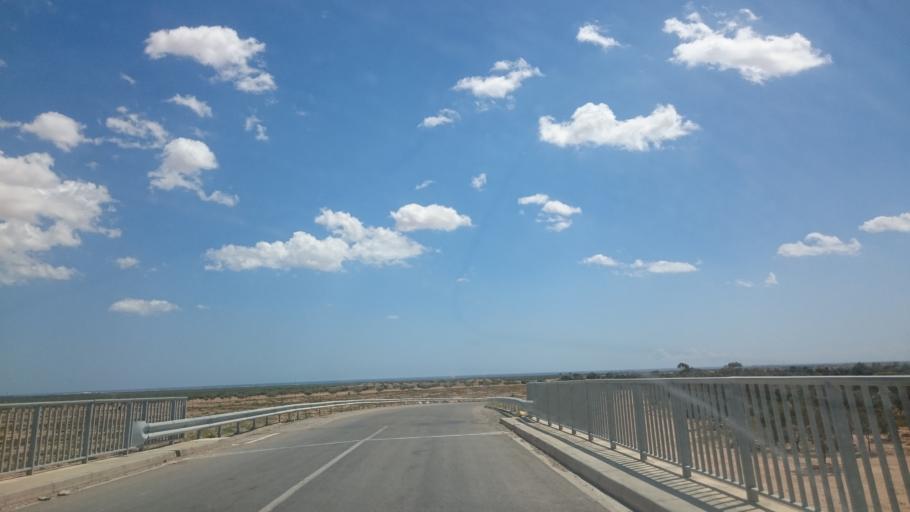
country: TN
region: Safaqis
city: Sfax
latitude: 34.6969
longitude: 10.5582
